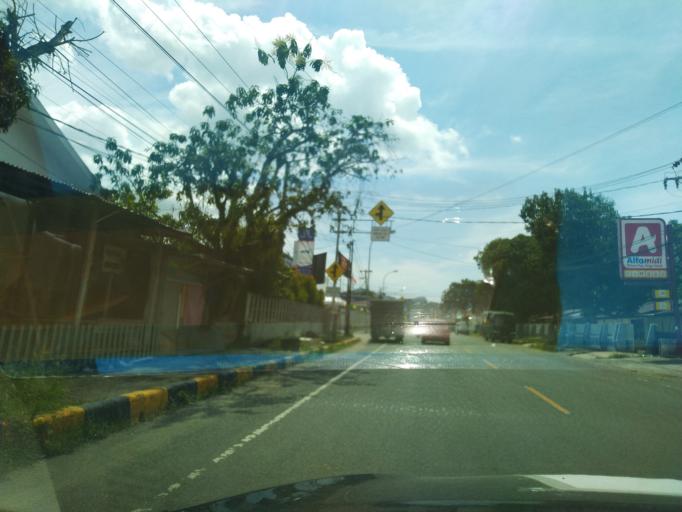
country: ID
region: Sulawesi Barat
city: Mamuju
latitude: -2.6796
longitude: 118.8777
